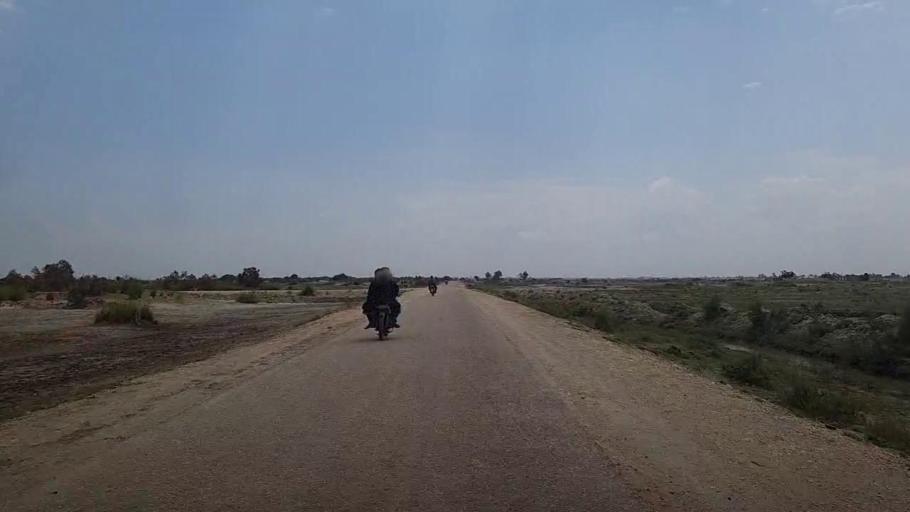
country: PK
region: Sindh
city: Kandhkot
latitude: 28.2913
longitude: 69.1432
